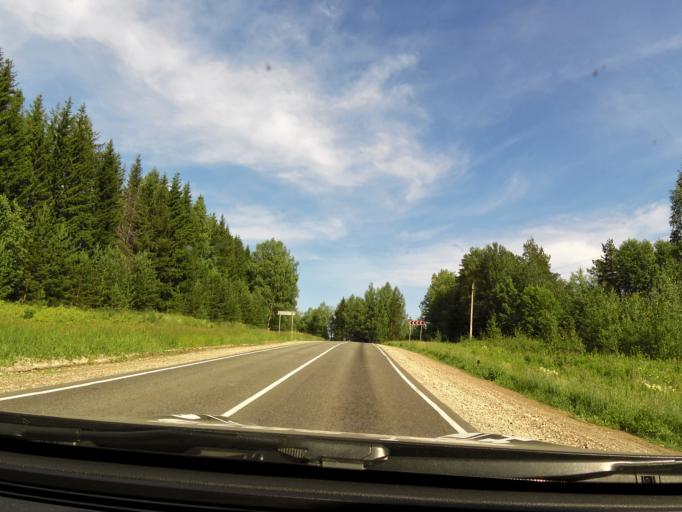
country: RU
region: Kirov
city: Belaya Kholunitsa
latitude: 58.8419
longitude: 50.6924
